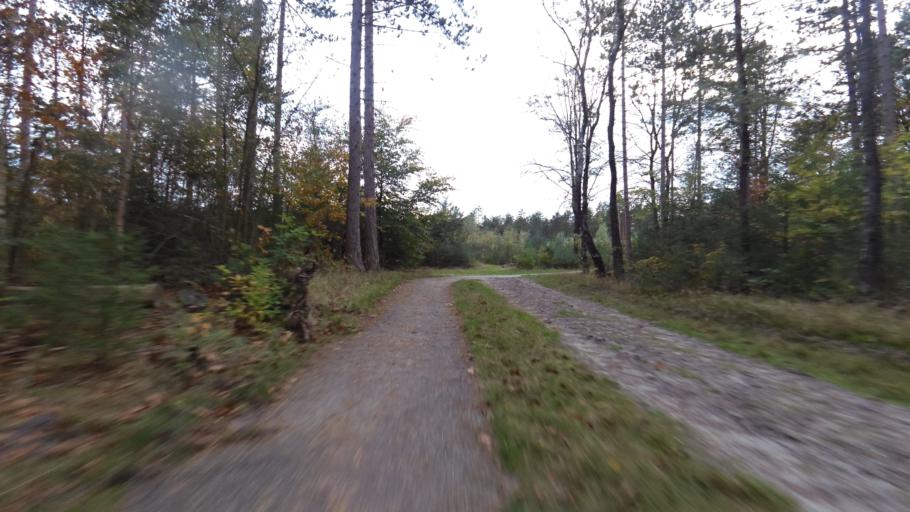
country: NL
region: Gelderland
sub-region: Gemeente Nunspeet
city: Nunspeet
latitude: 52.3777
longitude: 5.8335
